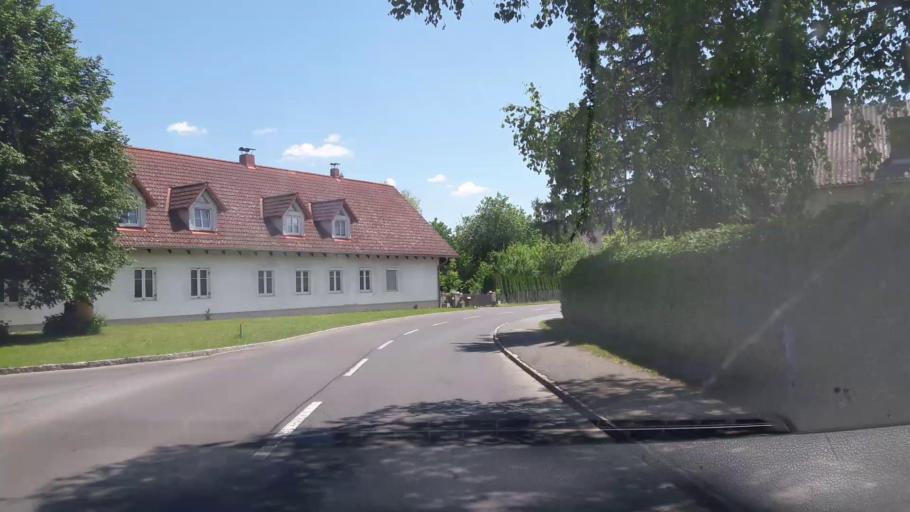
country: AT
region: Burgenland
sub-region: Politischer Bezirk Jennersdorf
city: Jennersdorf
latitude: 46.9523
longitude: 16.1193
